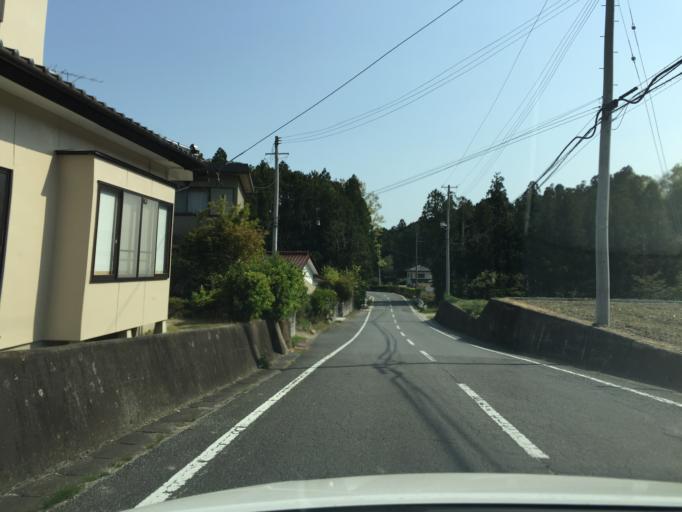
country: JP
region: Fukushima
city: Iwaki
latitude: 37.1415
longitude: 140.8542
